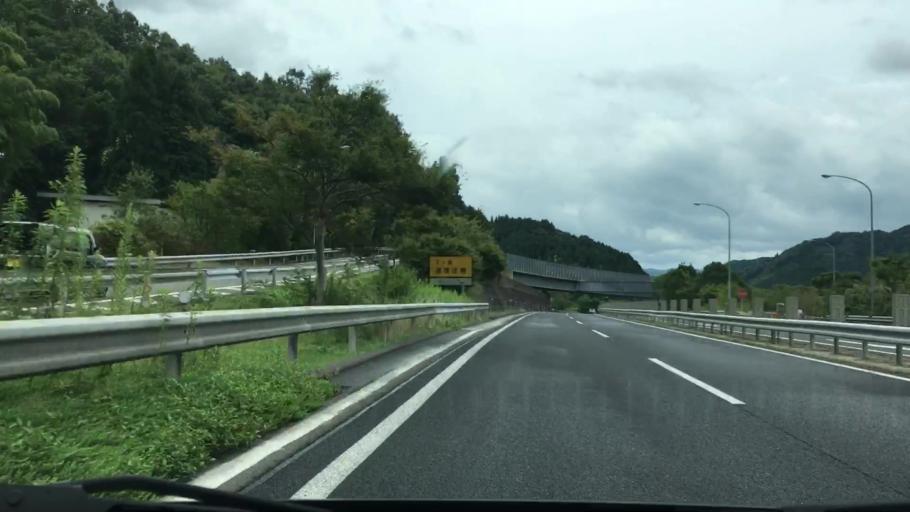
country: JP
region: Okayama
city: Tsuyama
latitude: 35.0527
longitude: 133.8101
